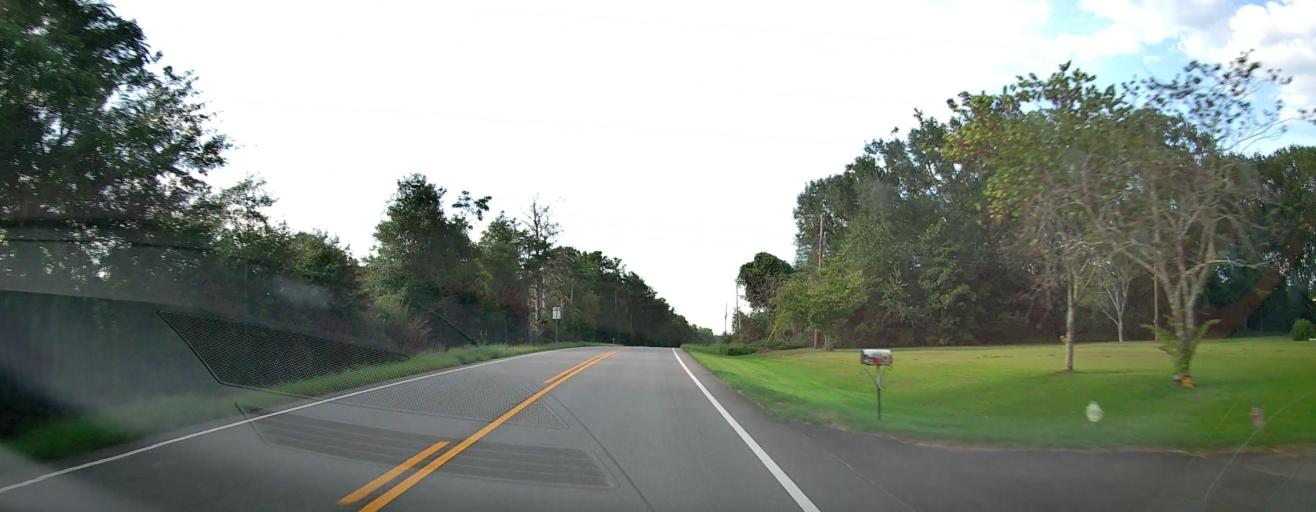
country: US
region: Georgia
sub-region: Monroe County
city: Forsyth
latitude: 32.9611
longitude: -83.9570
